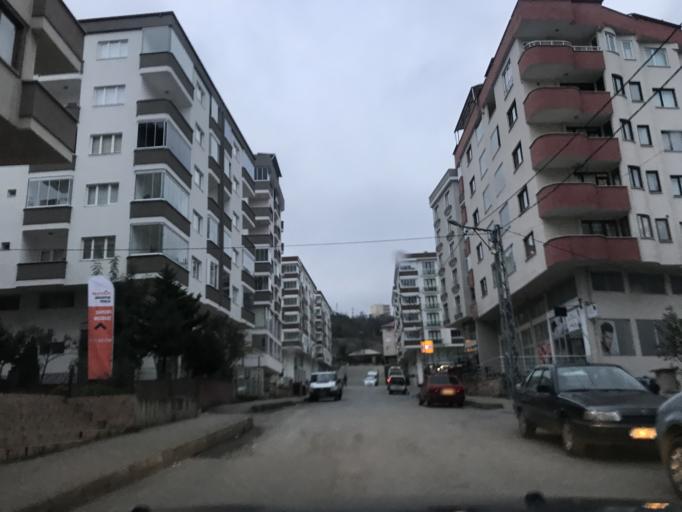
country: TR
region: Trabzon
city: Akcaabat
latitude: 41.0153
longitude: 39.5867
